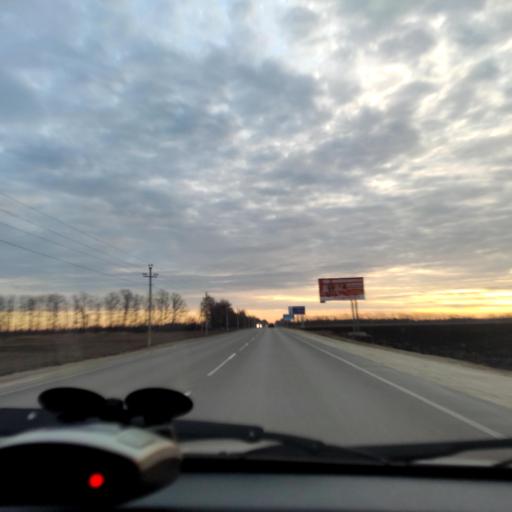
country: RU
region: Voronezj
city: Ramon'
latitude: 51.9291
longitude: 39.2300
